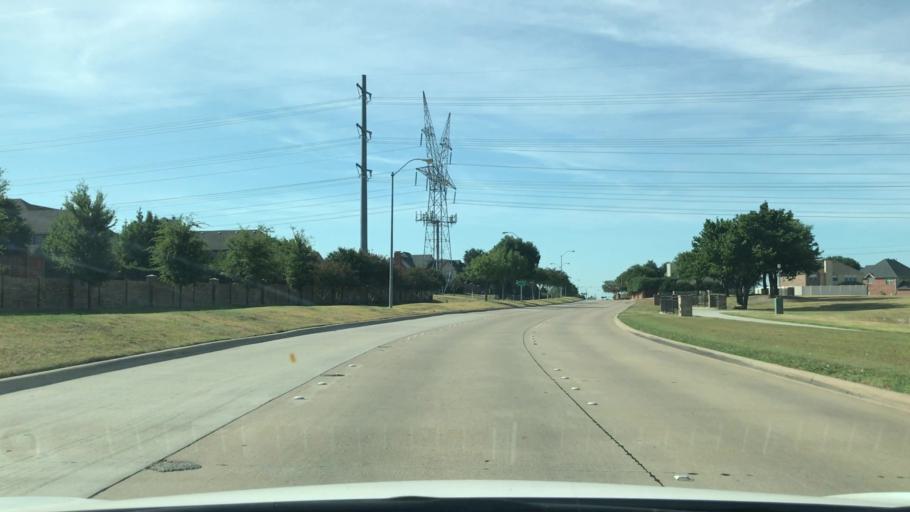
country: US
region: Texas
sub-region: Denton County
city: The Colony
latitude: 33.0606
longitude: -96.8389
